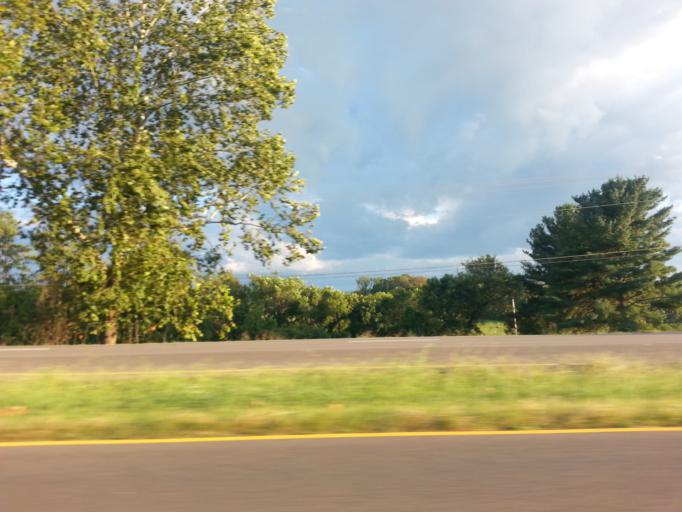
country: US
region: Tennessee
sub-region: Jefferson County
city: New Market
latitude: 36.1061
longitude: -83.5318
